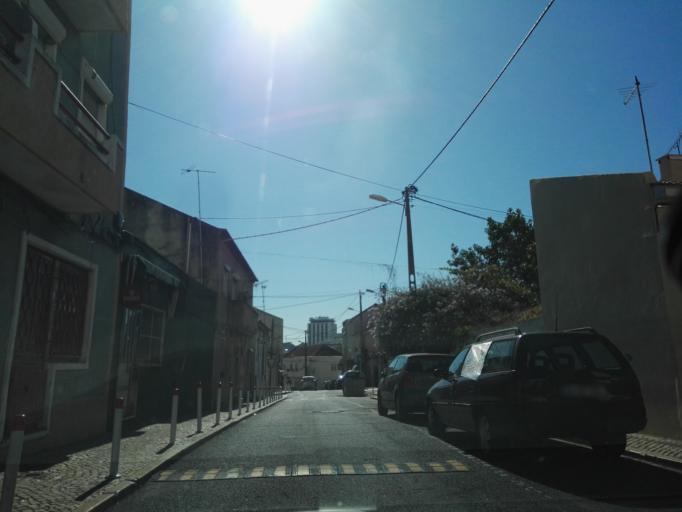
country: PT
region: Lisbon
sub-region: Loures
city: Sacavem
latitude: 38.7911
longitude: -9.1199
